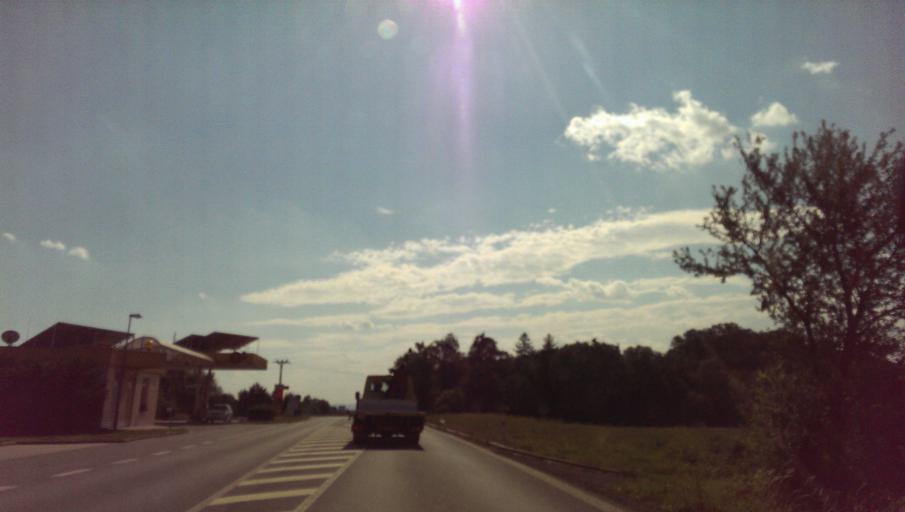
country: CZ
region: Zlin
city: Holesov
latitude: 49.3401
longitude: 17.5988
